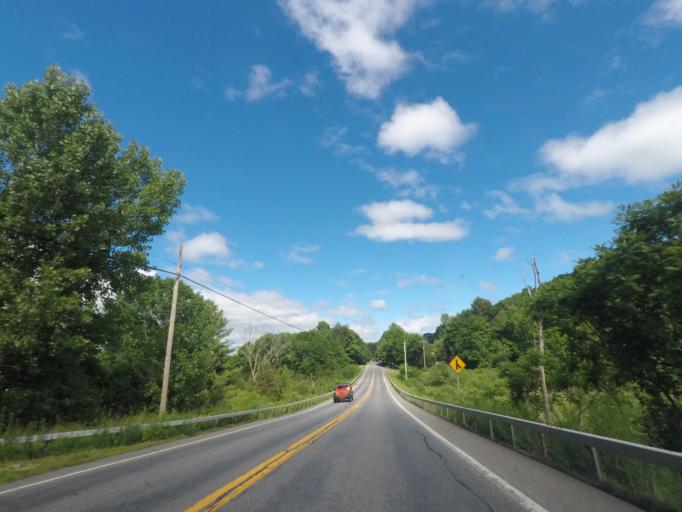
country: US
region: New York
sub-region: Columbia County
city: Philmont
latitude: 42.2092
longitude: -73.6504
